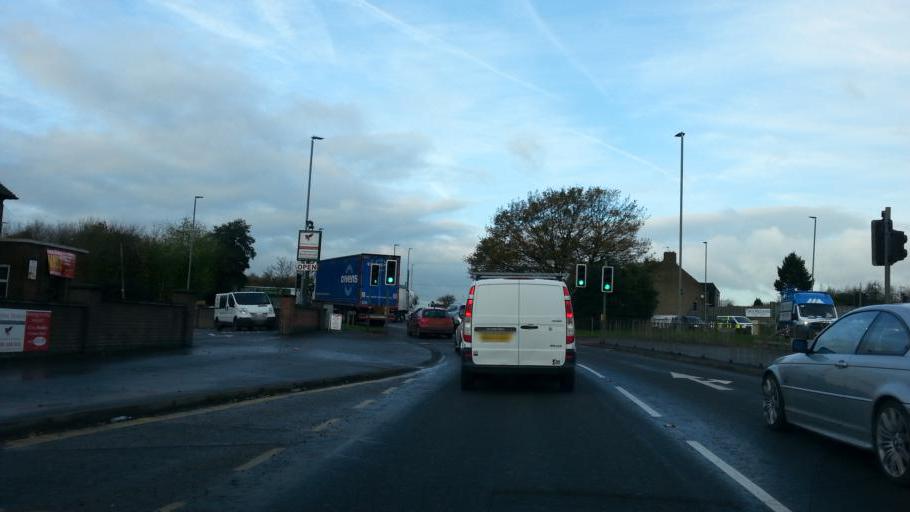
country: GB
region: England
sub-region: Leicestershire
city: Markfield
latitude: 52.7002
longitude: -1.3028
